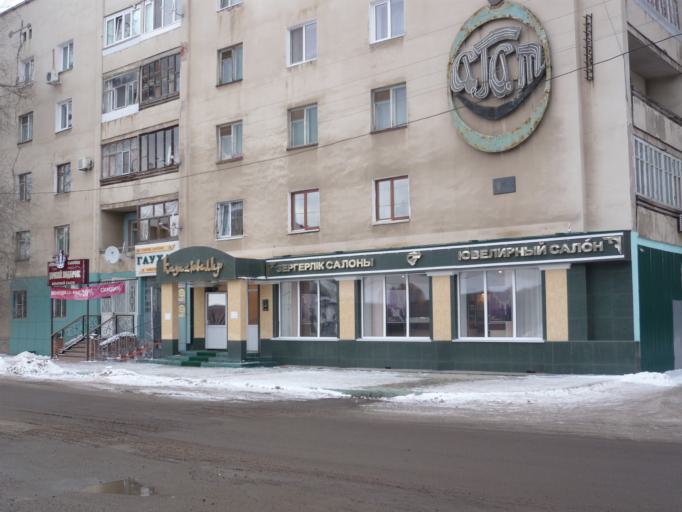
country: KZ
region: Batys Qazaqstan
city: Oral
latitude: 51.2093
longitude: 51.3670
